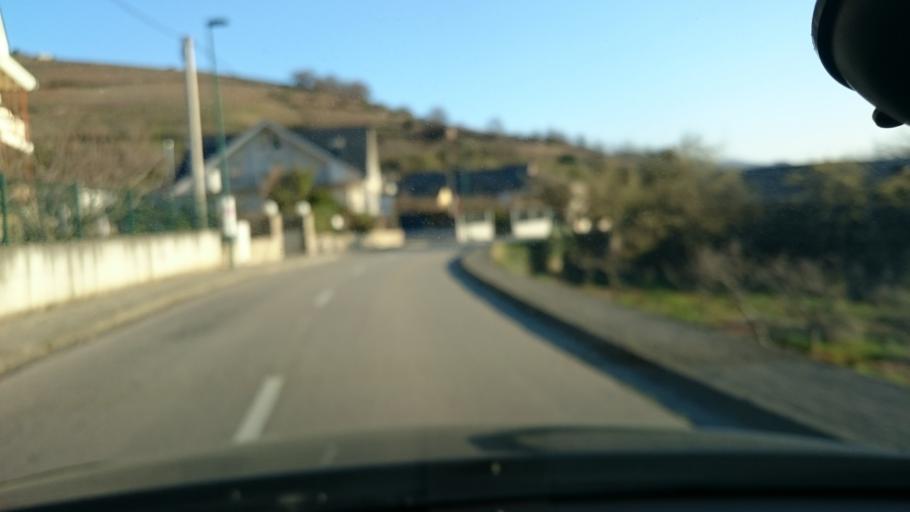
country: ES
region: Castille and Leon
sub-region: Provincia de Leon
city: Corullon
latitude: 42.5823
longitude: -6.8189
